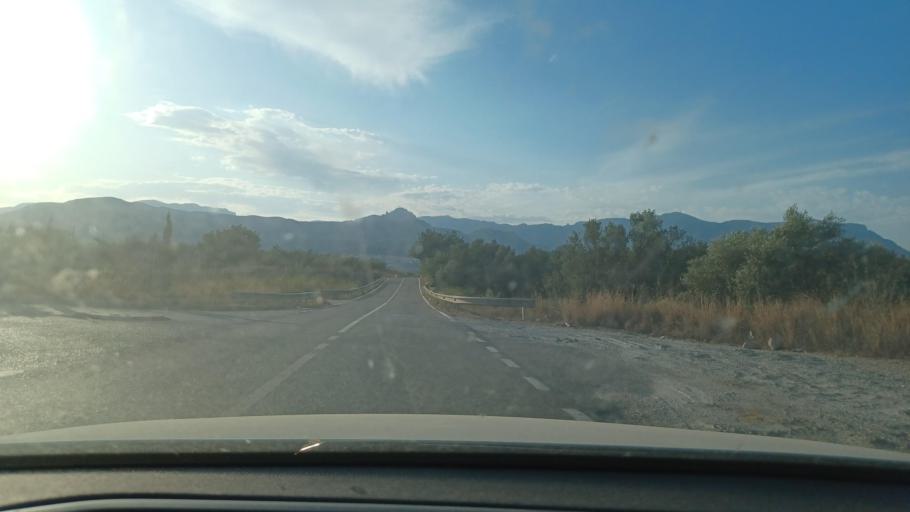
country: ES
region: Catalonia
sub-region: Provincia de Tarragona
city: Mas de Barberans
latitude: 40.7183
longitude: 0.4002
